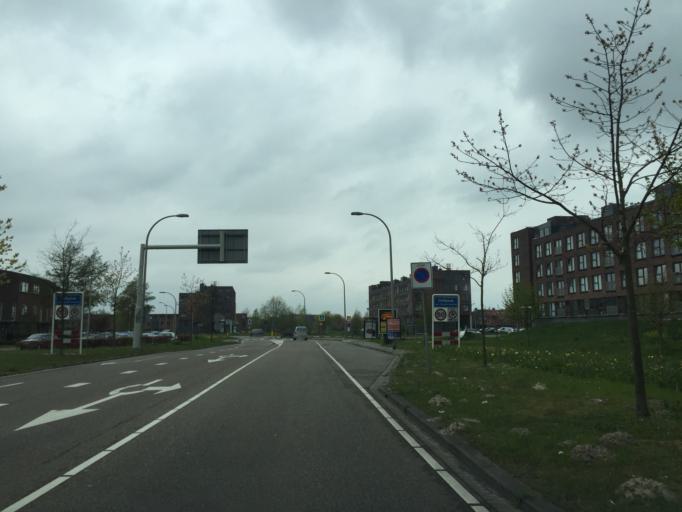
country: NL
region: South Holland
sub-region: Gemeente Pijnacker-Nootdorp
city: Pijnacker
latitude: 51.9985
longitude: 4.3972
